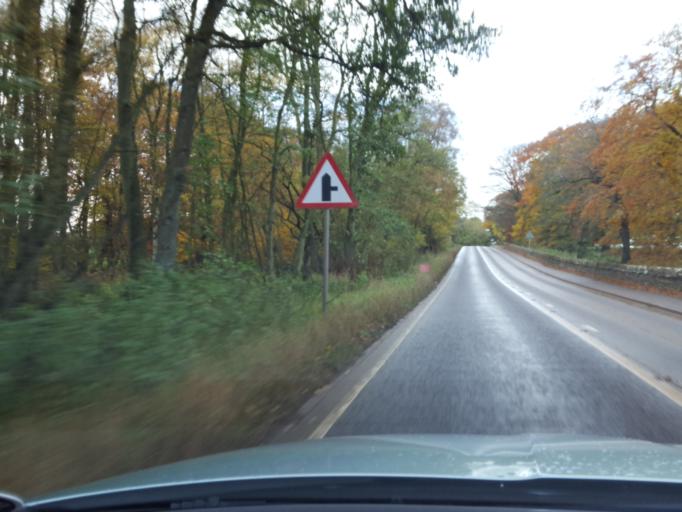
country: GB
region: Scotland
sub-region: South Lanarkshire
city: Carnwath
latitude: 55.7093
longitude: -3.6026
